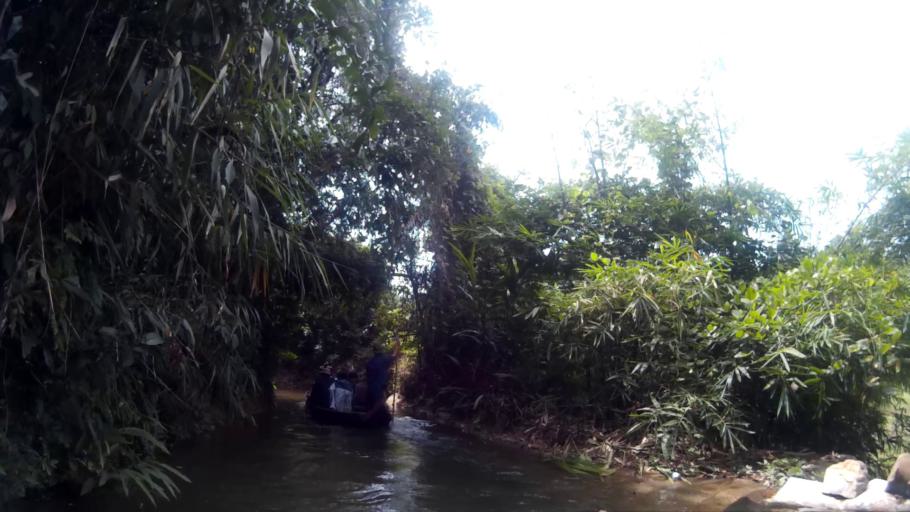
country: VN
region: Binh Dinh
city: Phu Phong
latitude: 13.8757
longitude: 108.8645
